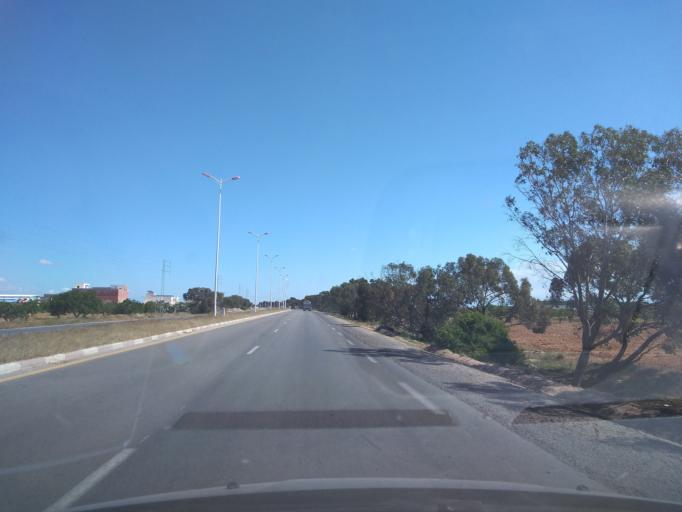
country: TN
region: Safaqis
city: Sfax
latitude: 34.8214
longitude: 10.7097
